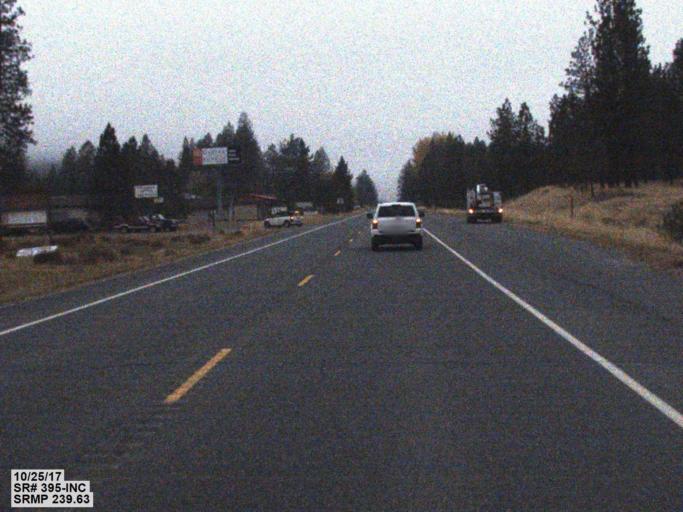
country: US
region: Washington
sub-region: Stevens County
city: Kettle Falls
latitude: 48.6081
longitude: -118.0848
